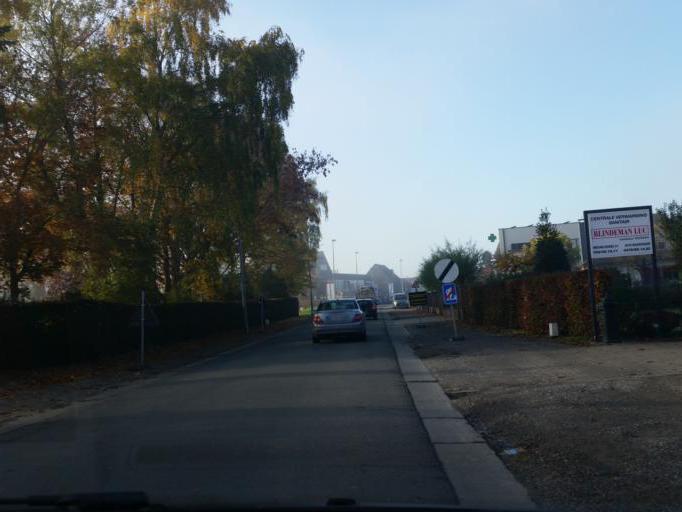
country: BE
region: Flanders
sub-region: Provincie Vlaams-Brabant
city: Opwijk
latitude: 50.9524
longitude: 4.1391
